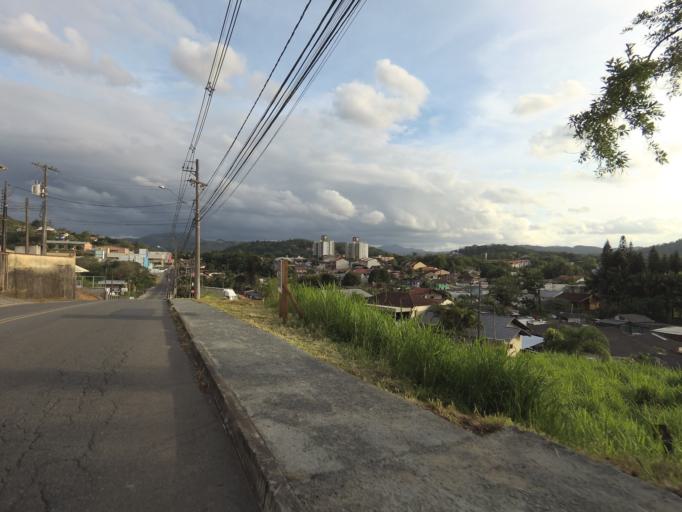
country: BR
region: Santa Catarina
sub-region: Blumenau
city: Blumenau
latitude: -26.9020
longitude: -49.1255
